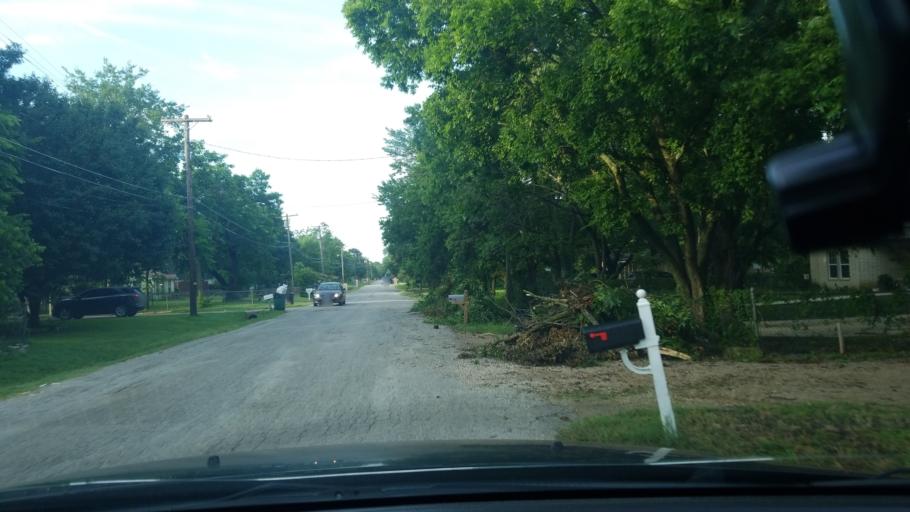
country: US
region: Texas
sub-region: Dallas County
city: Balch Springs
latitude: 32.7624
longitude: -96.6388
